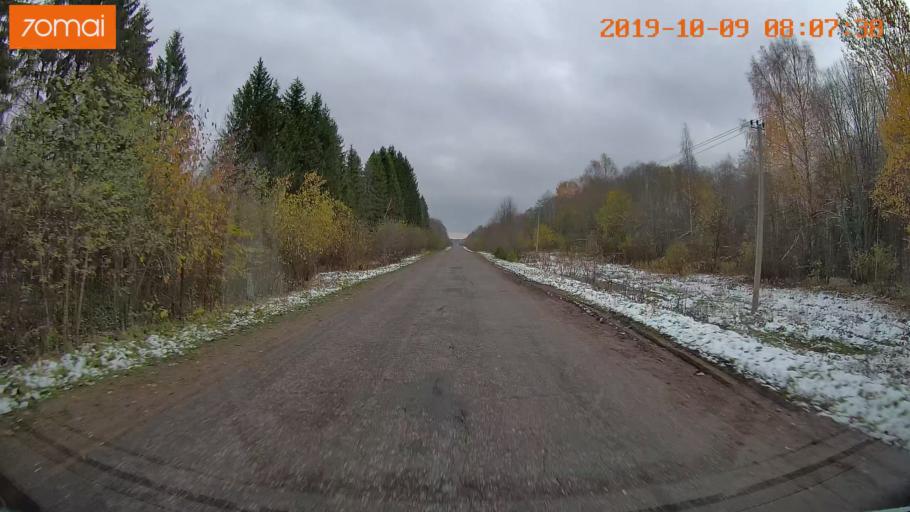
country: RU
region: Jaroslavl
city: Kukoboy
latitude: 58.6991
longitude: 40.0834
